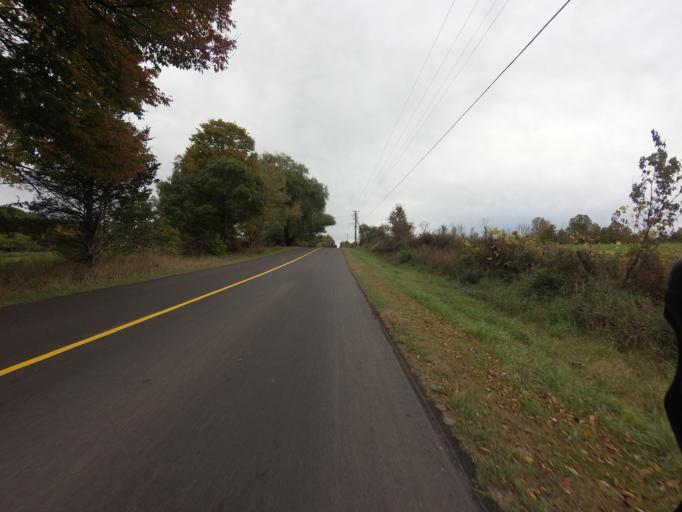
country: CA
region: Ontario
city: Gananoque
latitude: 44.5820
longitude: -76.0548
